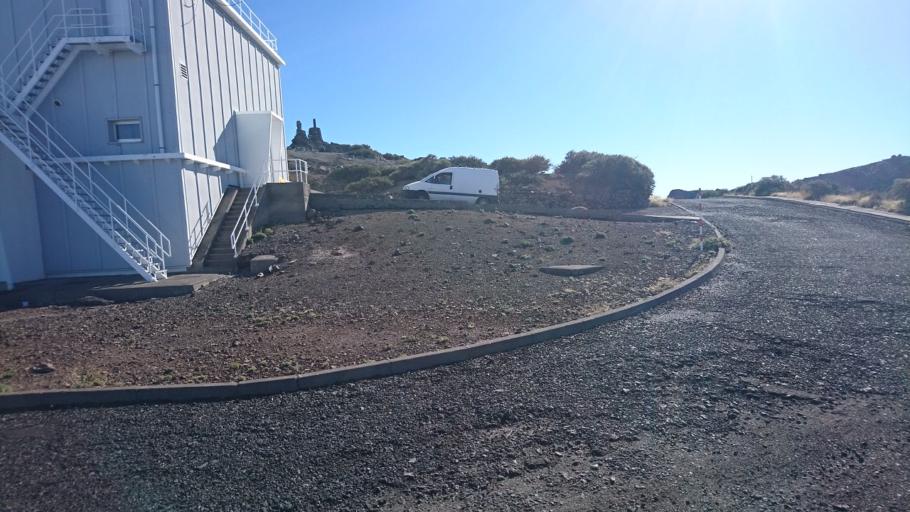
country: ES
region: Canary Islands
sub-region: Provincia de Santa Cruz de Tenerife
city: Garafia
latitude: 28.7614
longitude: -17.8782
